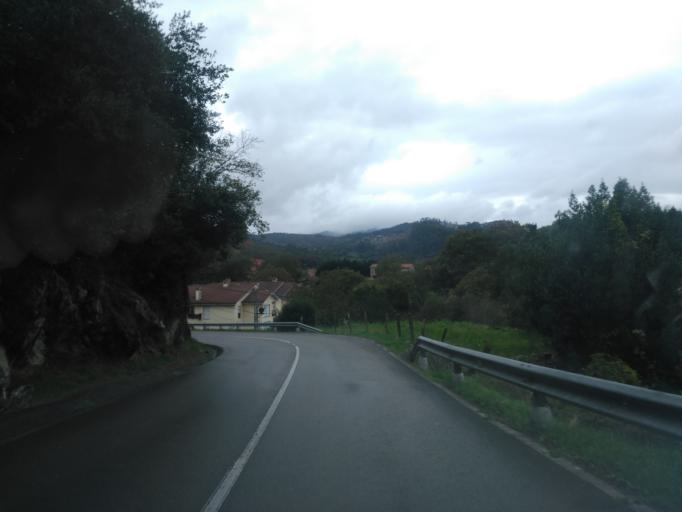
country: ES
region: Cantabria
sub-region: Provincia de Cantabria
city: Puente Viesgo
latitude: 43.2970
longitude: -3.9698
